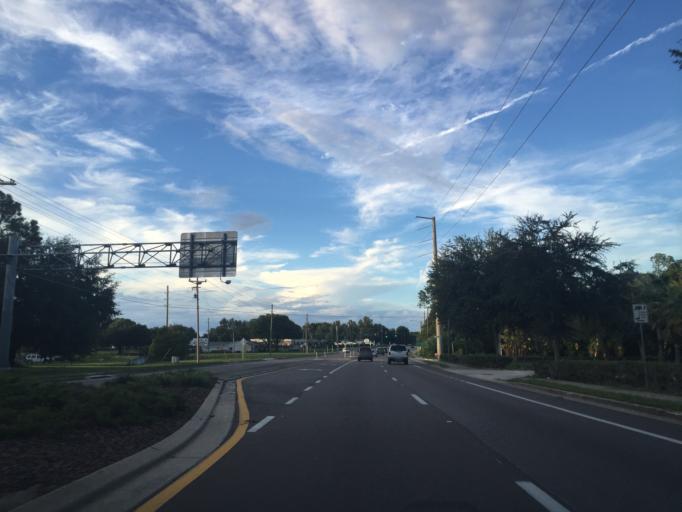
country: US
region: Florida
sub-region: Lake County
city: Tavares
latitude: 28.7875
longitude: -81.7475
